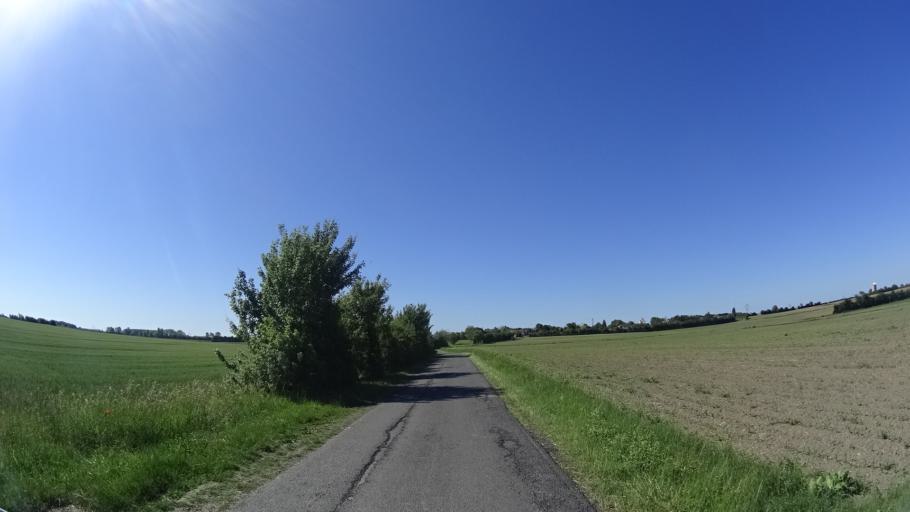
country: FR
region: Pays de la Loire
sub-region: Departement de Maine-et-Loire
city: Doue-la-Fontaine
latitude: 47.2404
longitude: -0.2924
